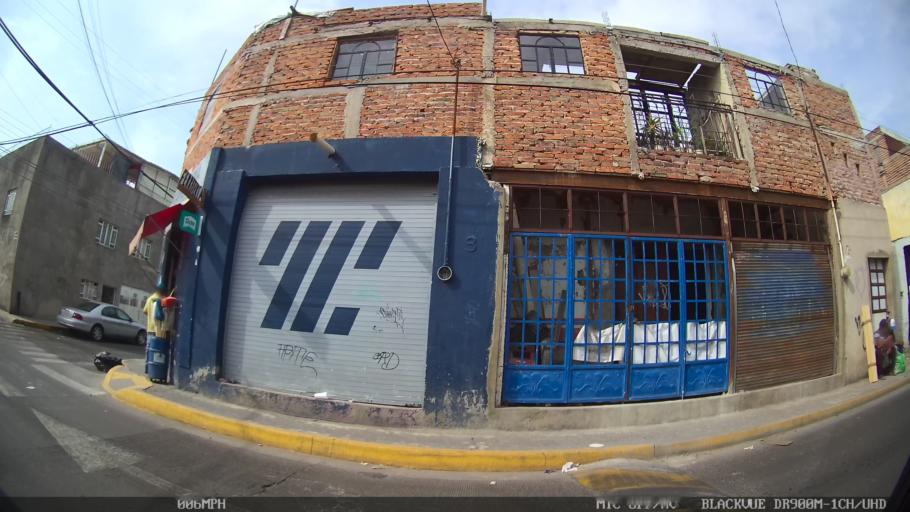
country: MX
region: Jalisco
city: Tonala
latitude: 20.6192
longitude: -103.2424
